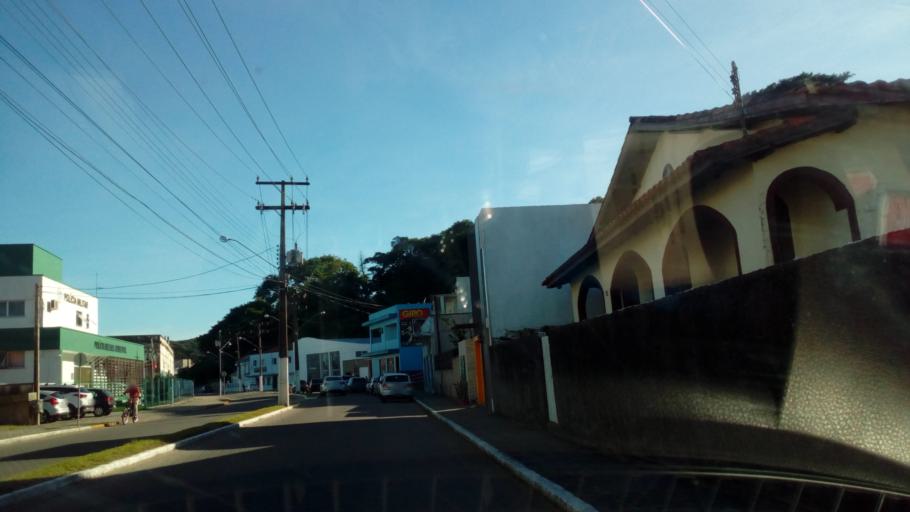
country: BR
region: Santa Catarina
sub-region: Laguna
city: Laguna
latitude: -28.4884
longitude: -48.7841
